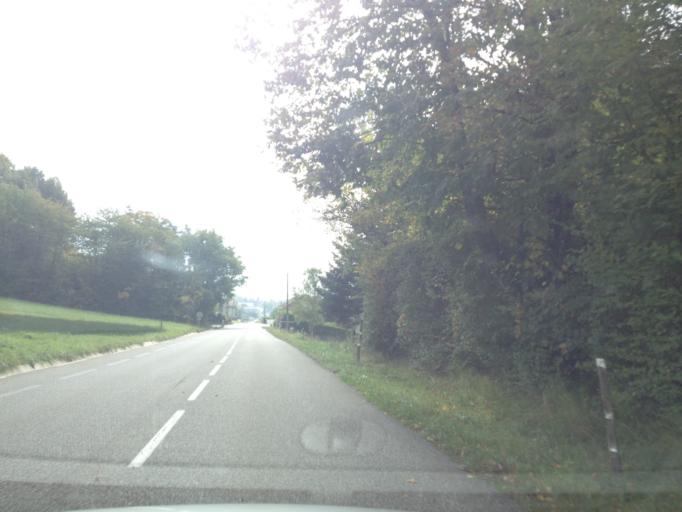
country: FR
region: Rhone-Alpes
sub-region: Departement de la Savoie
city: Mouxy
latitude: 45.6891
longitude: 5.9392
